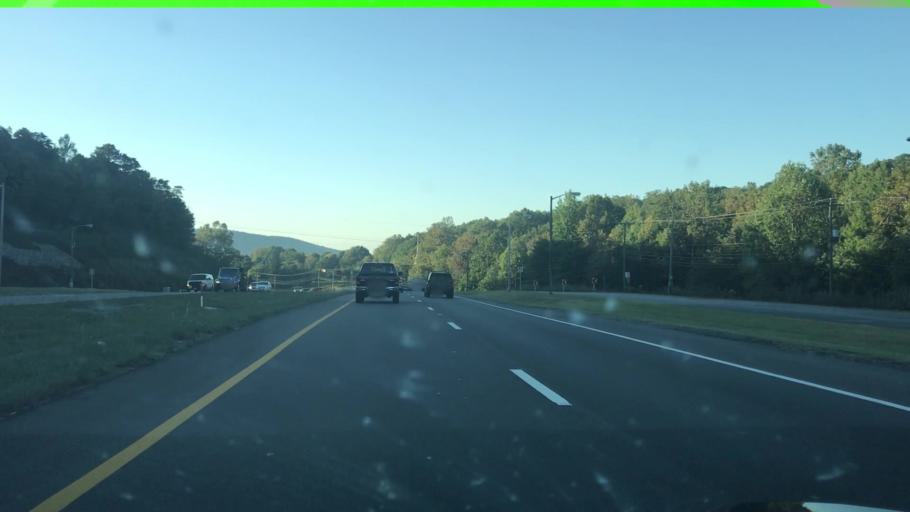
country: US
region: Virginia
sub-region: Botetourt County
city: Cloverdale
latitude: 37.3485
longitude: -79.8830
